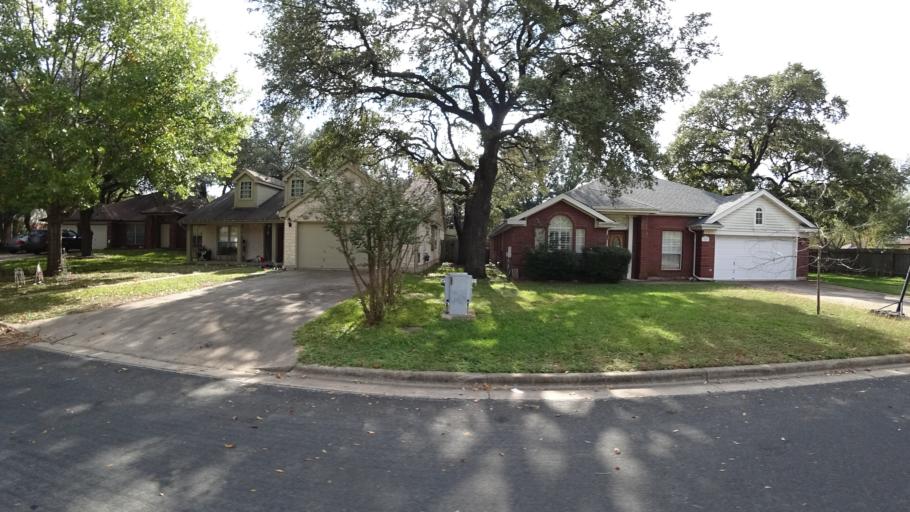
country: US
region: Texas
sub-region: Travis County
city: Shady Hollow
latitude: 30.1602
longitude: -97.8531
